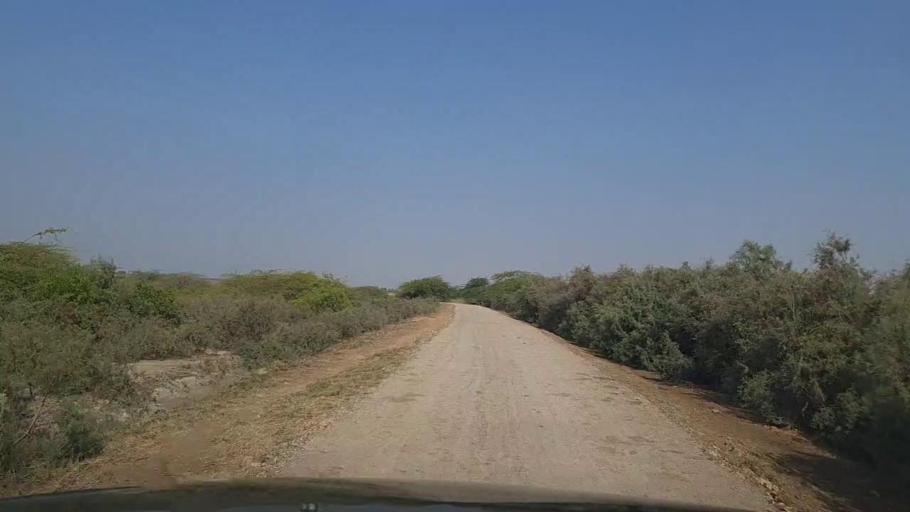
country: PK
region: Sindh
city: Thatta
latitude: 24.6481
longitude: 67.8170
